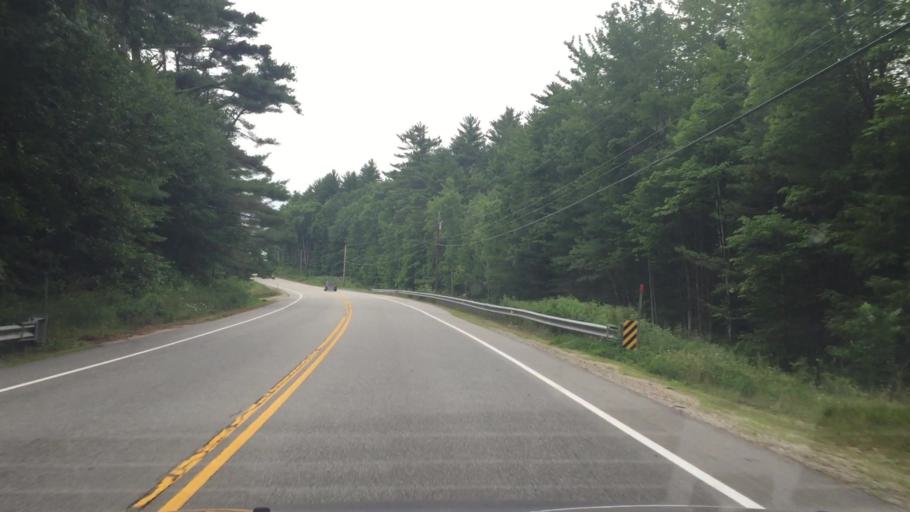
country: US
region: New Hampshire
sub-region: Carroll County
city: Moultonborough
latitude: 43.7799
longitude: -71.3801
